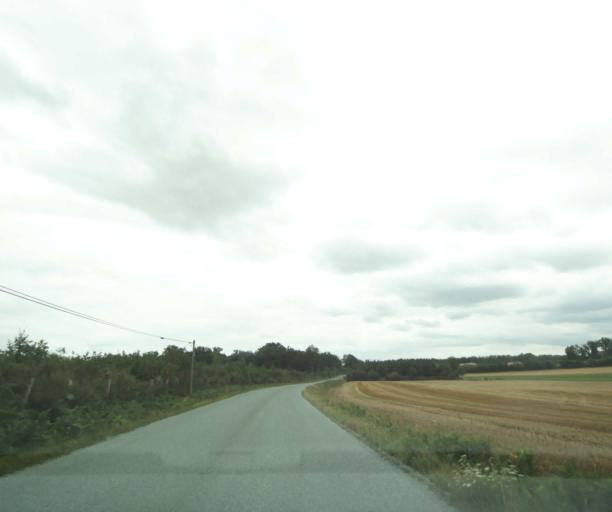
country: FR
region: Pays de la Loire
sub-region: Departement de Maine-et-Loire
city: Durtal
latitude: 47.7005
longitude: -0.2659
